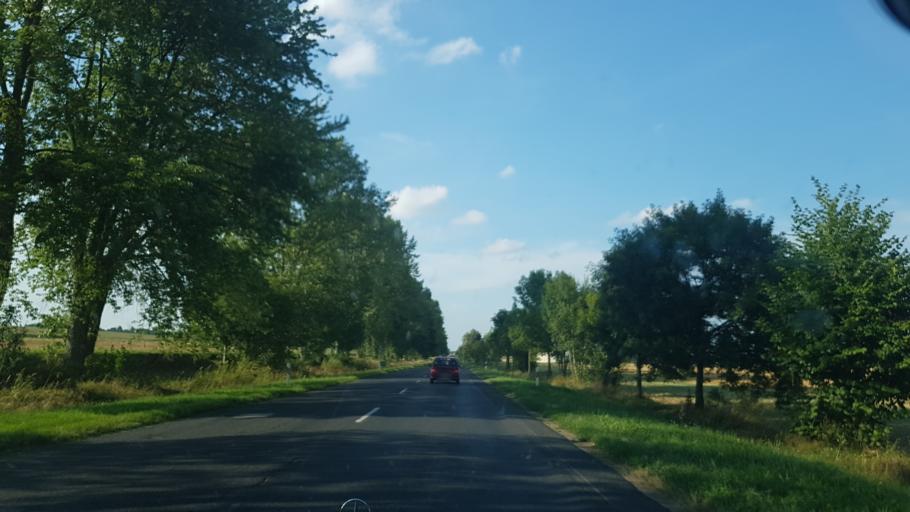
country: HU
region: Somogy
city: Nagyatad
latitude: 46.2685
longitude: 17.3588
